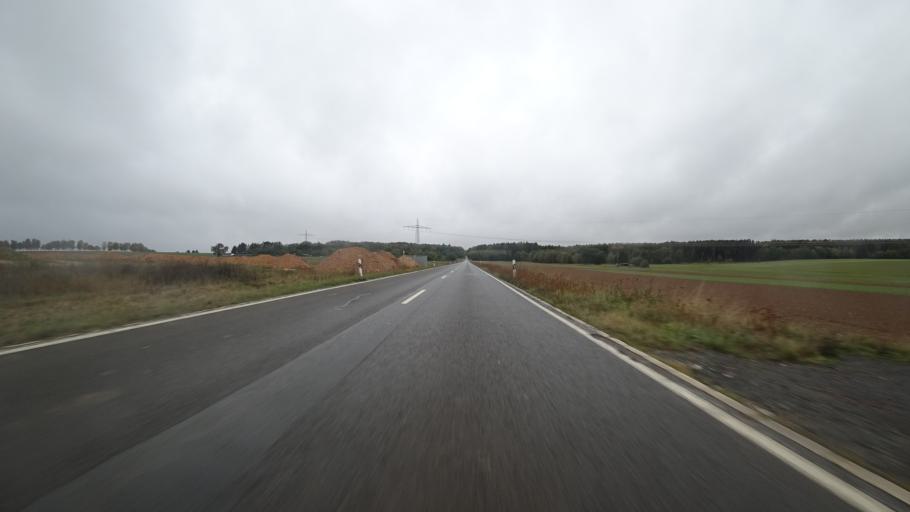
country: DE
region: Rheinland-Pfalz
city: Rheinbollen
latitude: 50.0090
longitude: 7.6589
